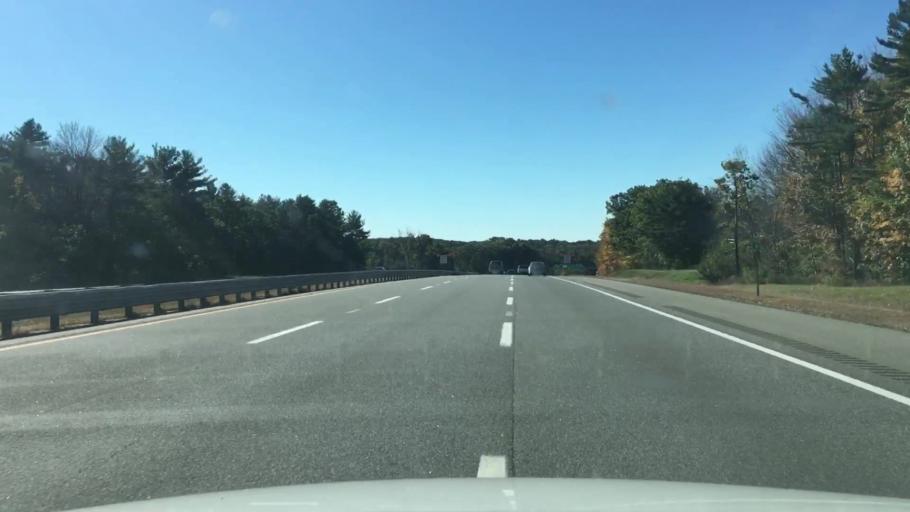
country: US
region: Maine
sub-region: York County
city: York Harbor
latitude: 43.1685
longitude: -70.6531
